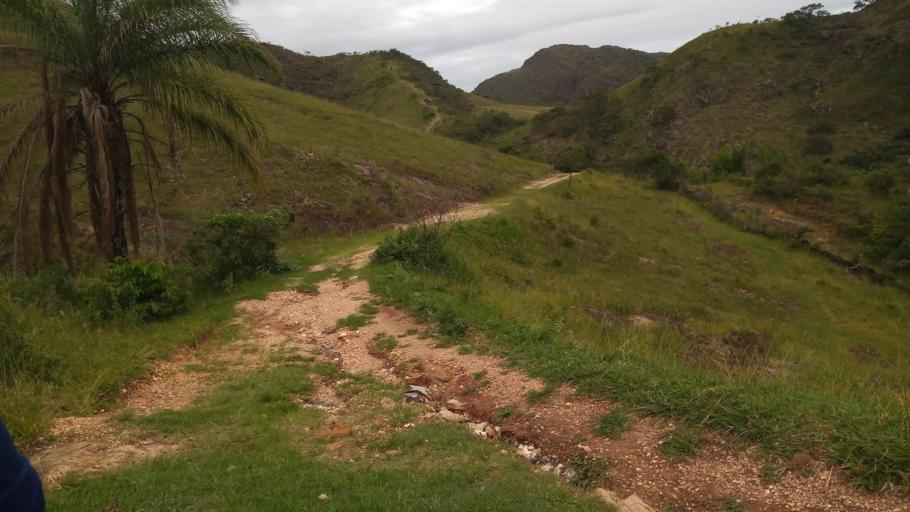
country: BR
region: Minas Gerais
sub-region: Sao Joao Del Rei
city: Sao Joao del Rei
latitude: -21.1255
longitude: -44.2692
